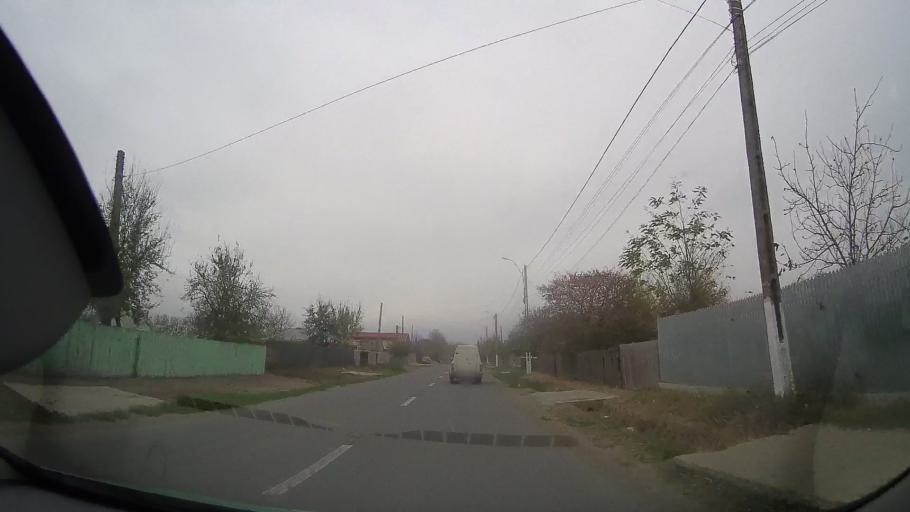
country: RO
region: Braila
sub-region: Comuna Budesti
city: Tataru
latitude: 44.8531
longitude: 27.4229
